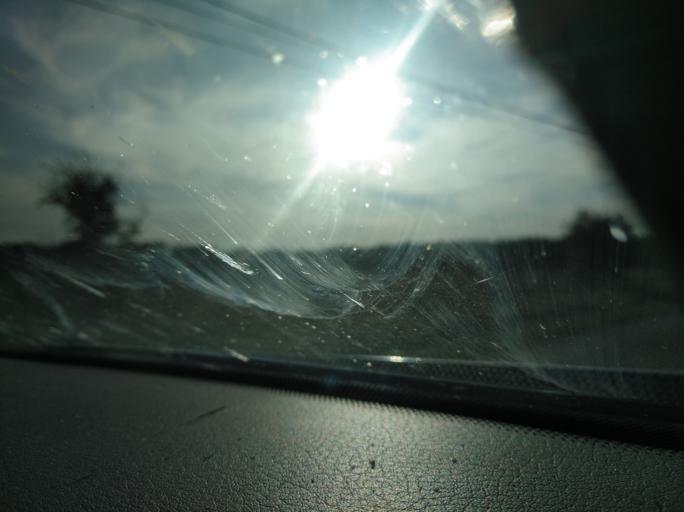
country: PT
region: Evora
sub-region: Borba
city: Borba
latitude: 38.9454
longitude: -7.4839
